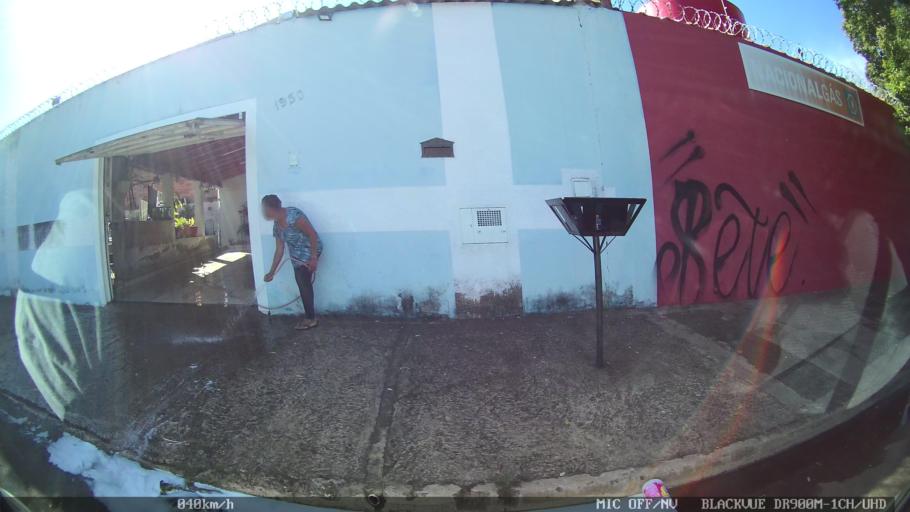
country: BR
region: Sao Paulo
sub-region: Franca
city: Franca
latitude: -20.4909
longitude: -47.4218
